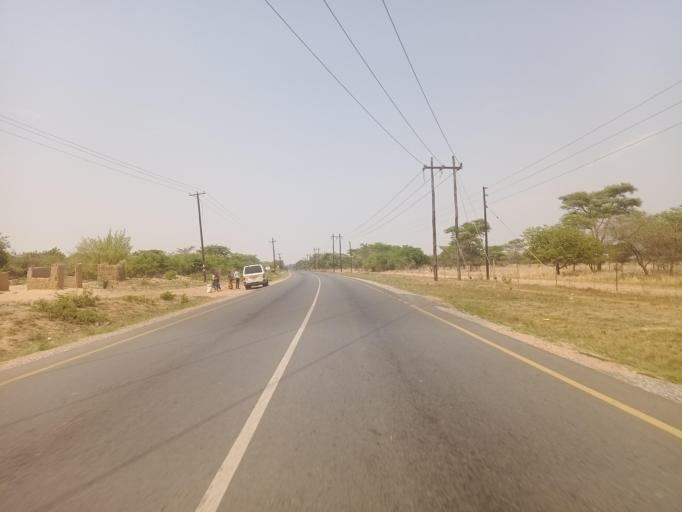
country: ZM
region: Lusaka
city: Lusaka
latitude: -15.2815
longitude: 28.3904
